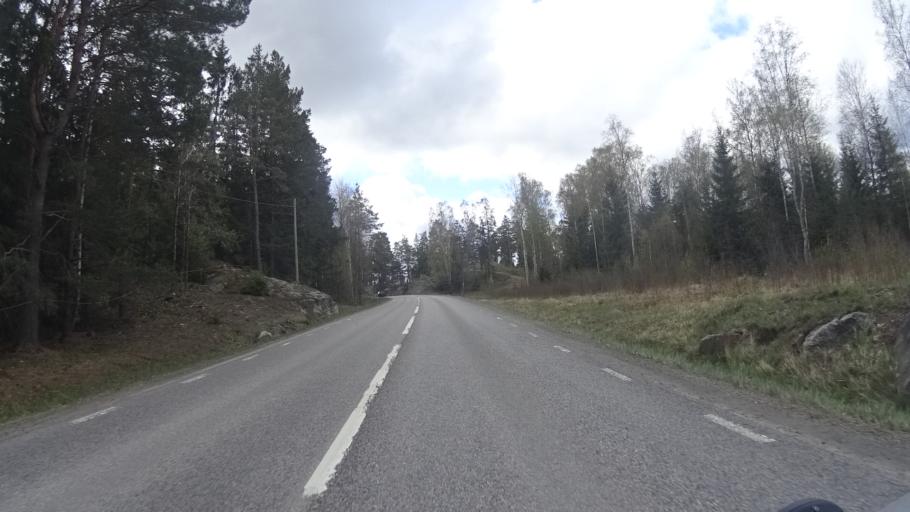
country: SE
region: Stockholm
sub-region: Botkyrka Kommun
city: Tullinge
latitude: 59.1804
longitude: 17.9284
